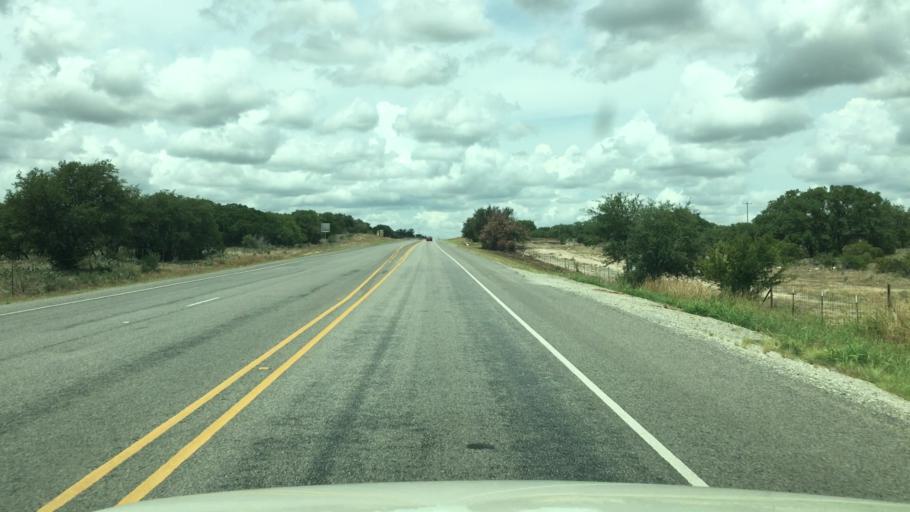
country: US
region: Texas
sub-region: McCulloch County
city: Brady
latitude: 31.0304
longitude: -99.2294
